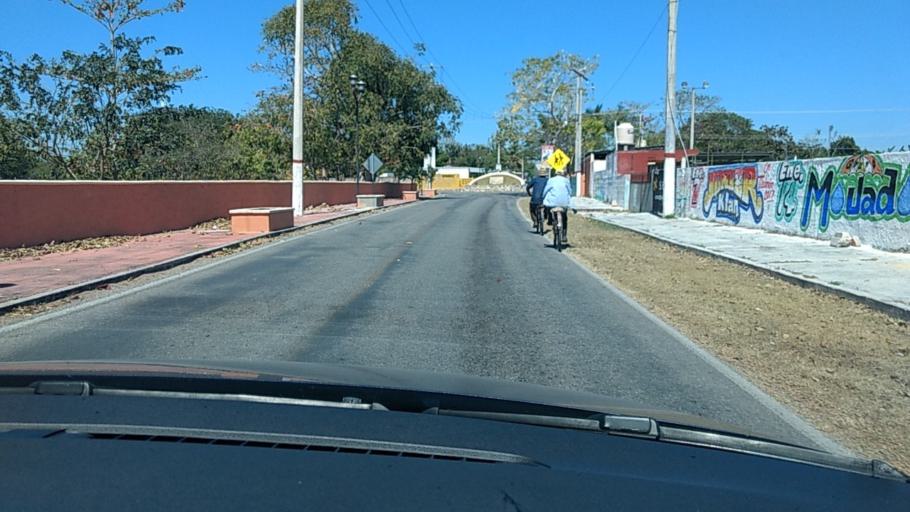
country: MX
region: Yucatan
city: Panaba
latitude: 21.2893
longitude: -88.2707
